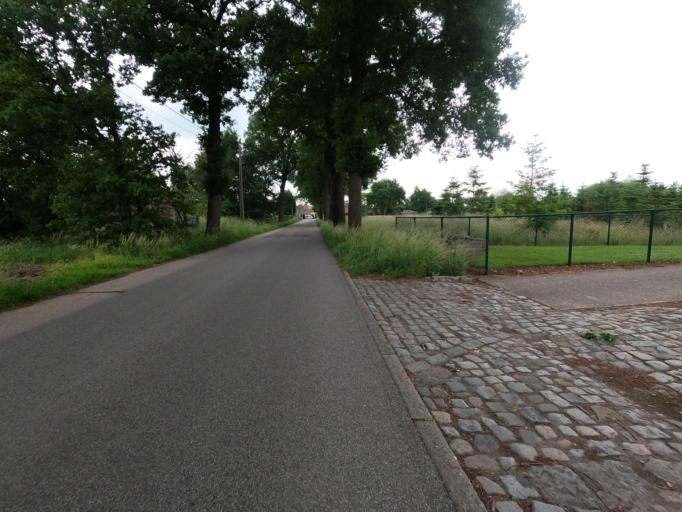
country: BE
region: Flanders
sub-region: Provincie Antwerpen
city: Kalmthout
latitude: 51.4255
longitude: 4.4985
